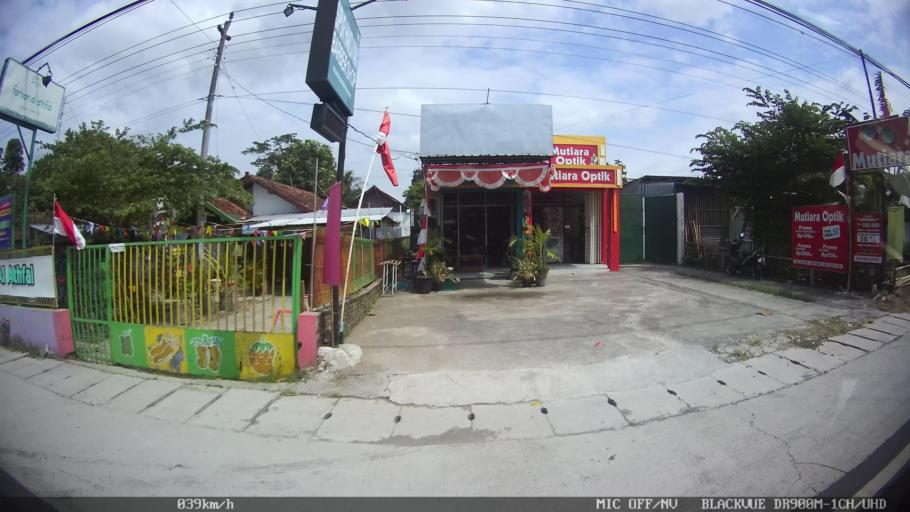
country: ID
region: Central Java
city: Candi Prambanan
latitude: -7.8171
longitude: 110.4813
